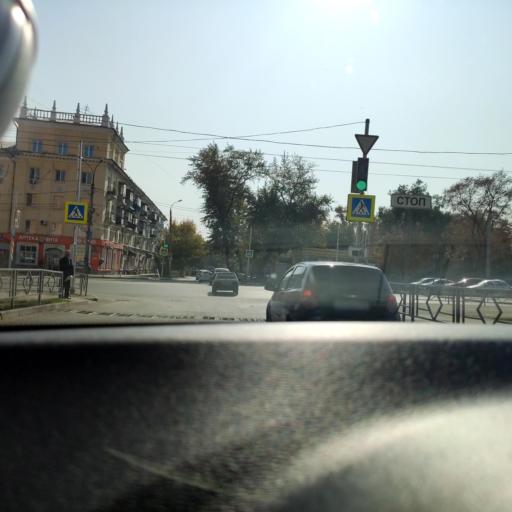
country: RU
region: Samara
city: Samara
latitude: 53.2042
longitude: 50.2191
